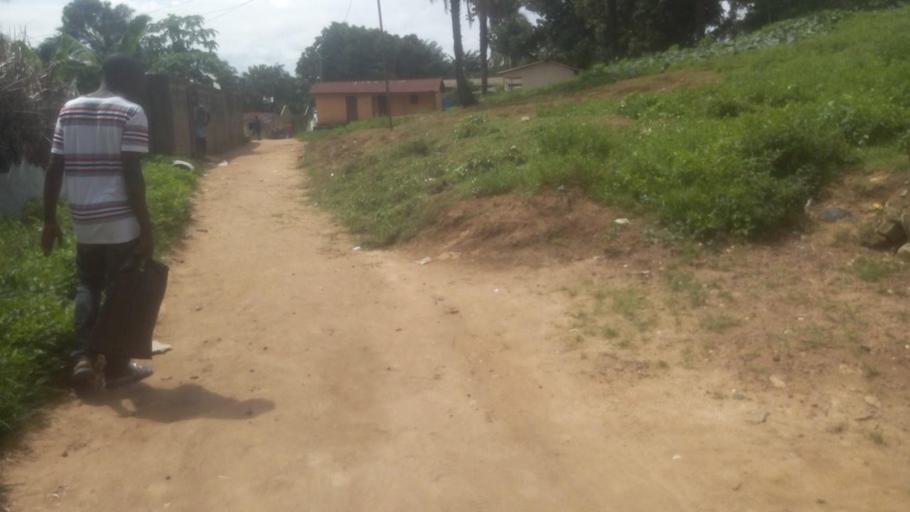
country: SL
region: Western Area
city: Freetown
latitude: 8.5209
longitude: -13.1500
